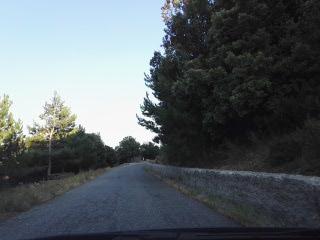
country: IT
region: Calabria
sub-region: Provincia di Vibo-Valentia
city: Nardodipace
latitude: 38.4196
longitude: 16.3515
